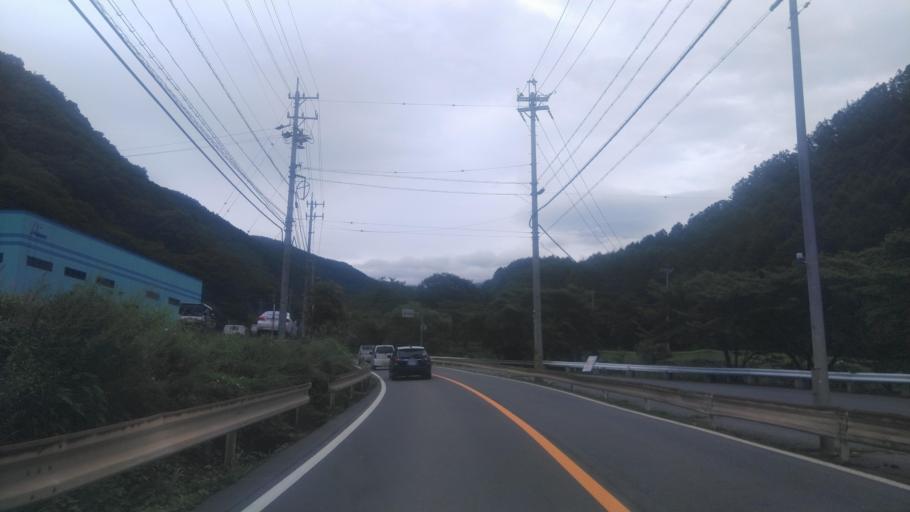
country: JP
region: Nagano
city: Ueda
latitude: 36.4685
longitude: 138.3422
